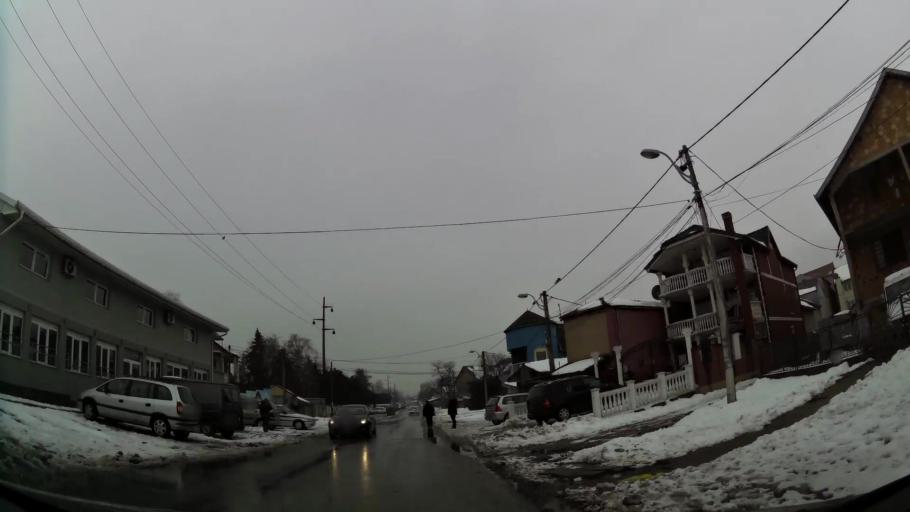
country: RS
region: Central Serbia
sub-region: Belgrade
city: Zemun
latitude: 44.8464
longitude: 20.3731
